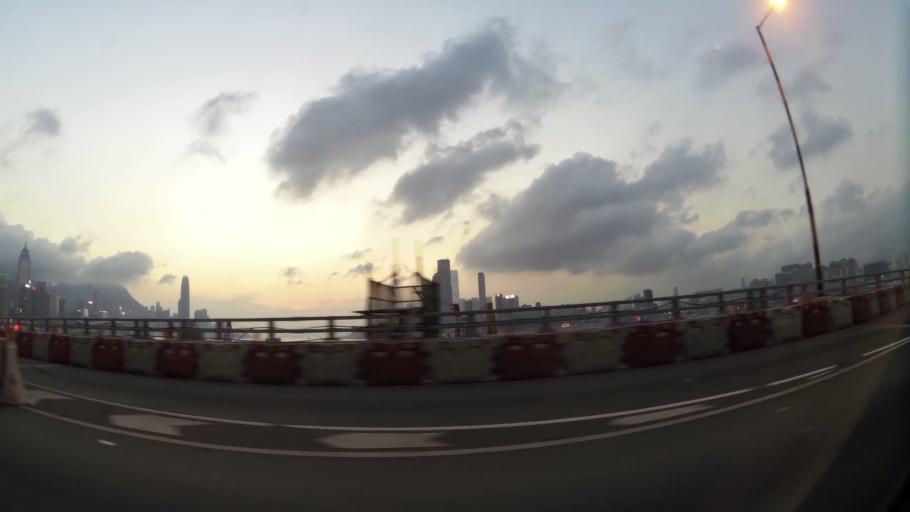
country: HK
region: Wanchai
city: Wan Chai
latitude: 22.2884
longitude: 114.1898
